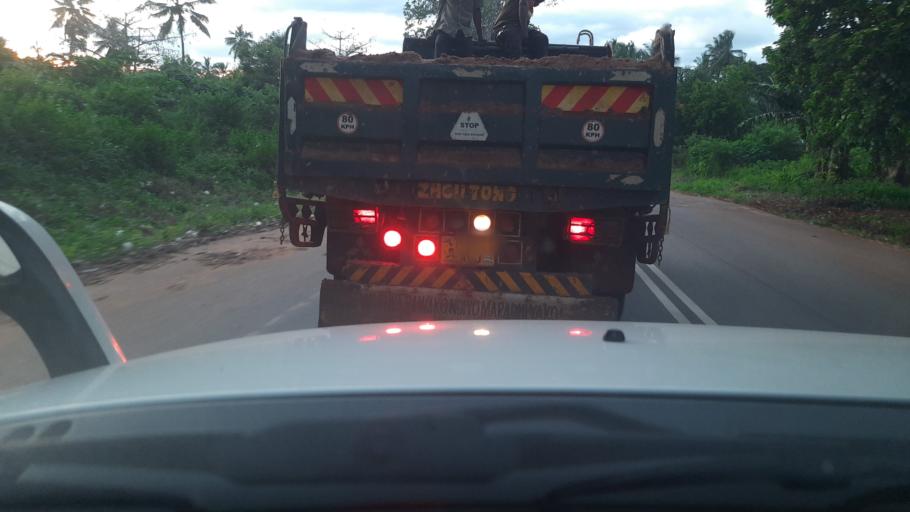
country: TZ
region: Tanga
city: Muheza
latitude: -5.1795
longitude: 38.8212
